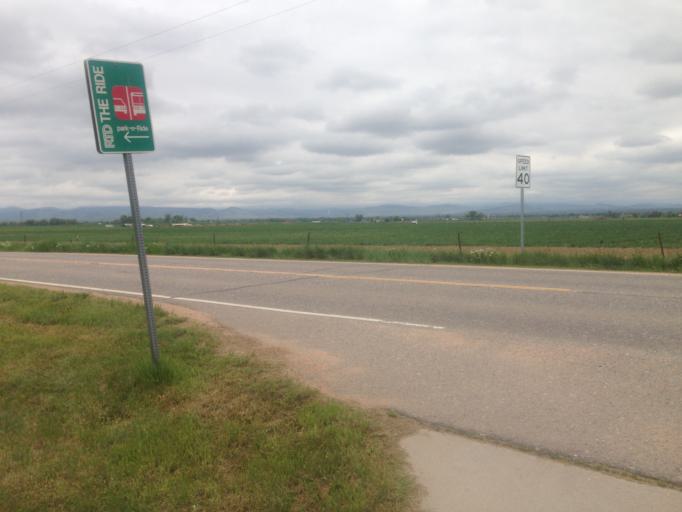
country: US
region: Colorado
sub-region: Boulder County
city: Longmont
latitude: 40.1022
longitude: -105.1040
